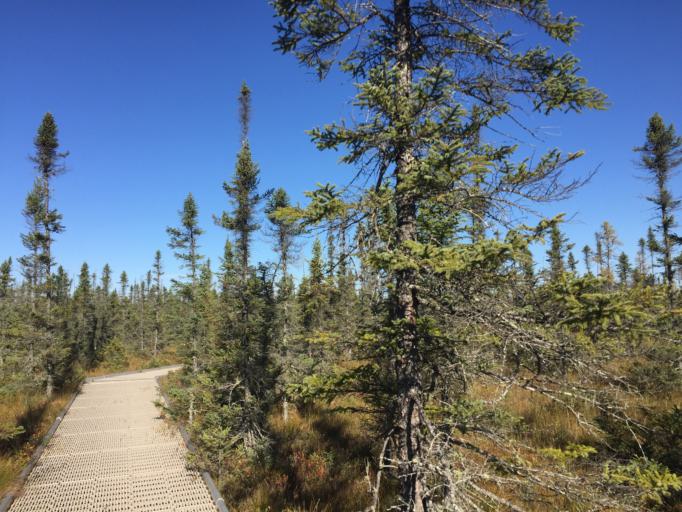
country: US
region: Minnesota
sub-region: Lake of the Woods County
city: Baudette
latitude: 48.2972
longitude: -94.5670
